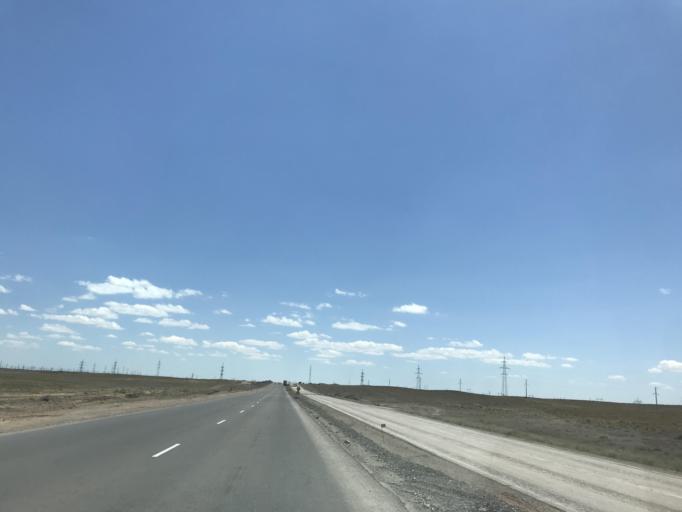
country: KZ
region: Almaty Oblysy
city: Ulken
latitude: 45.2190
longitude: 73.8630
